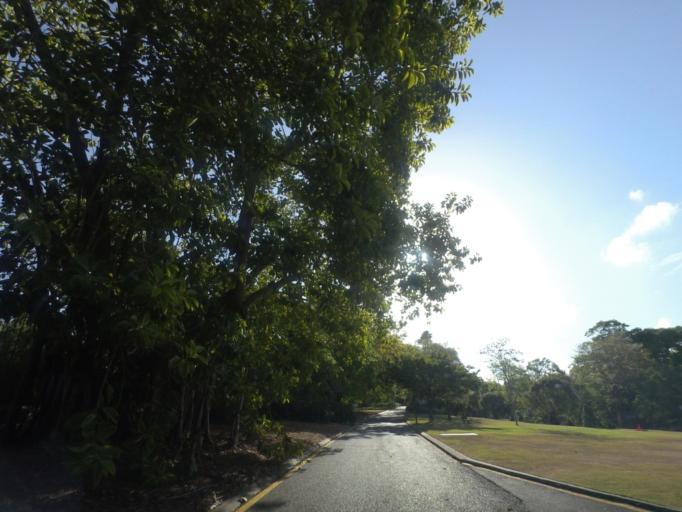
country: AU
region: Queensland
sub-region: Brisbane
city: Taringa
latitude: -27.4776
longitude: 152.9768
